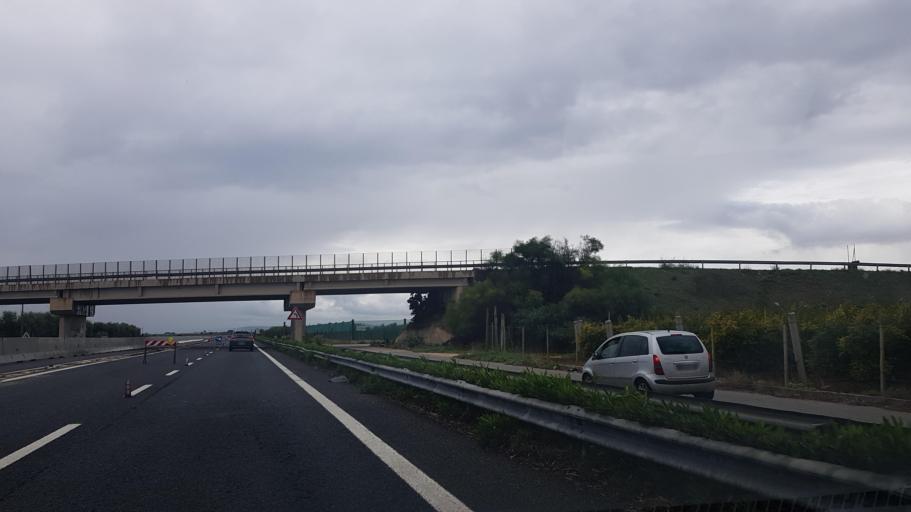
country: IT
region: Apulia
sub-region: Provincia di Taranto
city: Massafra
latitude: 40.5302
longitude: 17.1146
